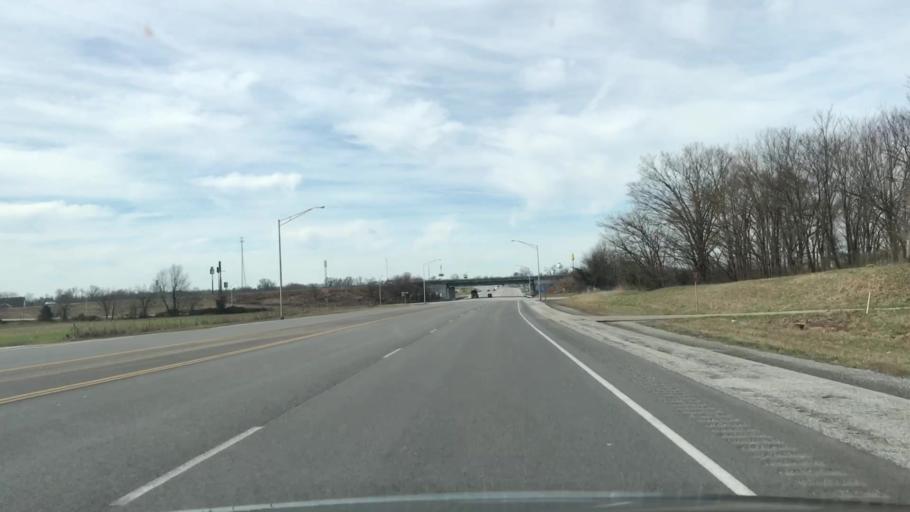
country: US
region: Kentucky
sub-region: Trigg County
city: Cadiz
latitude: 36.8850
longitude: -87.7332
